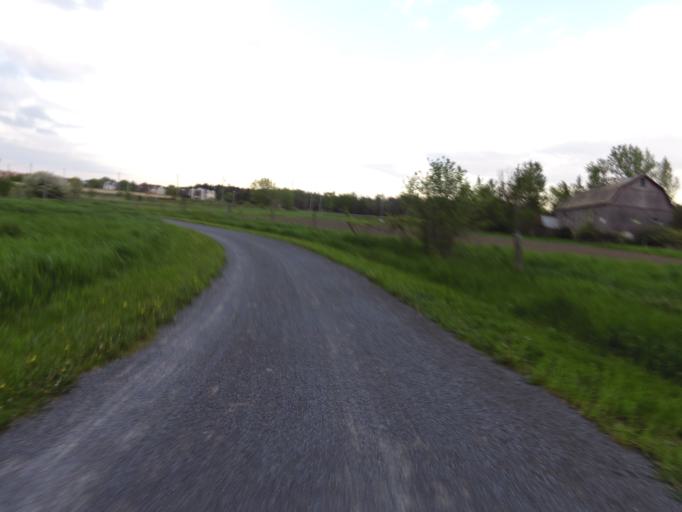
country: CA
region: Ontario
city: Bells Corners
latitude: 45.3175
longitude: -75.8494
